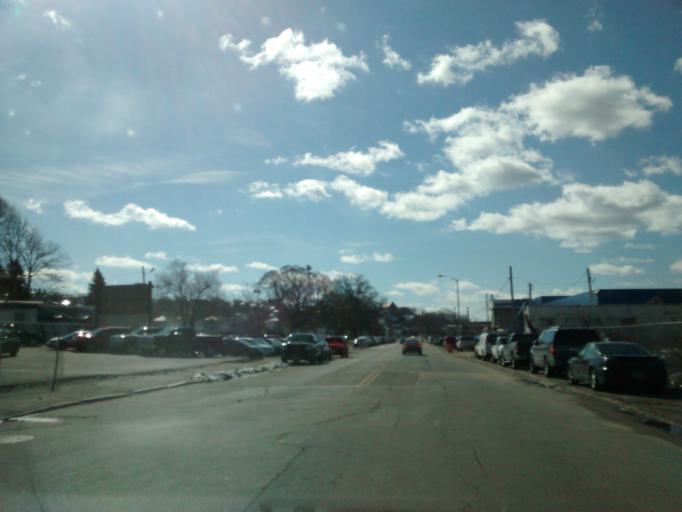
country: US
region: Massachusetts
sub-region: Worcester County
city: Worcester
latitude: 42.2515
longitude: -71.8054
